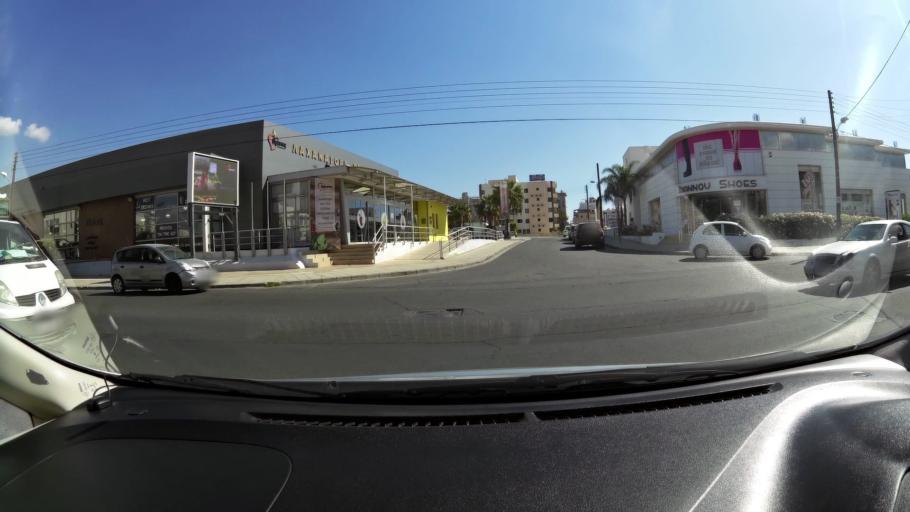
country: CY
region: Larnaka
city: Larnaca
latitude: 34.9290
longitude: 33.6330
